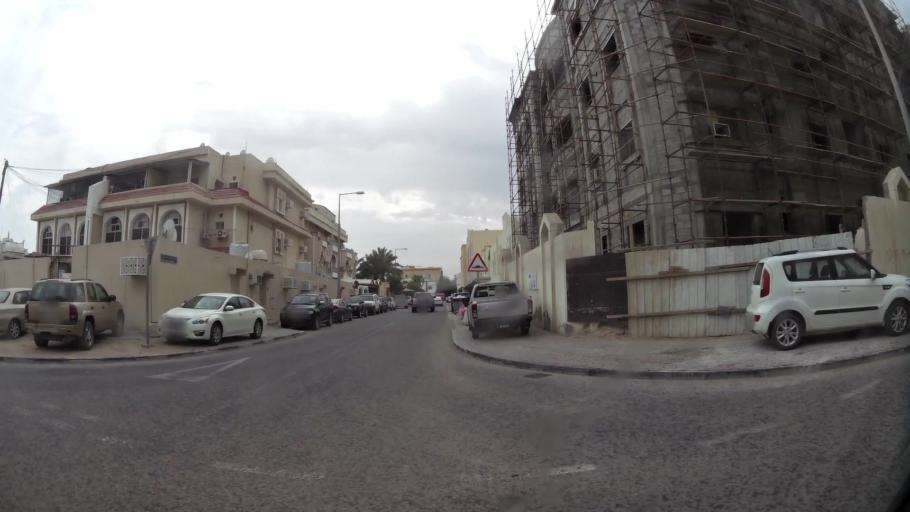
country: QA
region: Baladiyat ad Dawhah
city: Doha
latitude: 25.2750
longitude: 51.4928
